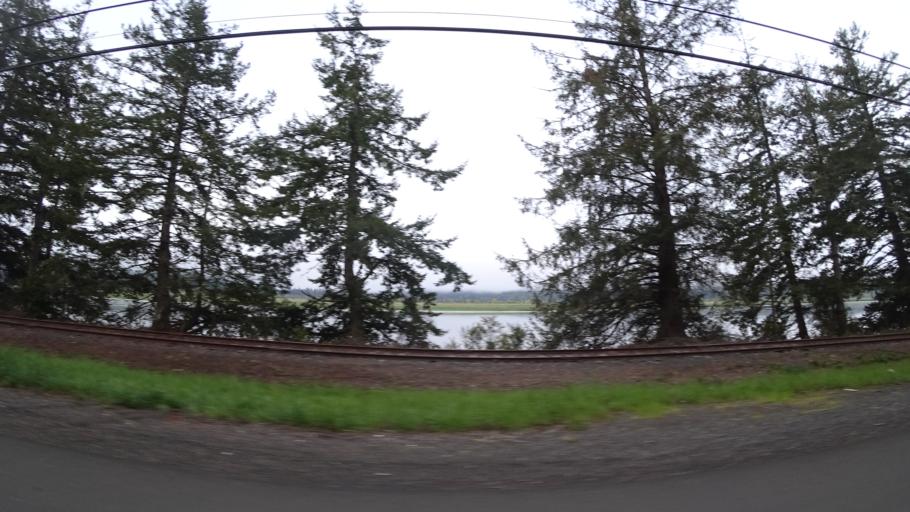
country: US
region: Oregon
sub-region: Douglas County
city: Reedsport
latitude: 43.7229
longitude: -124.1090
